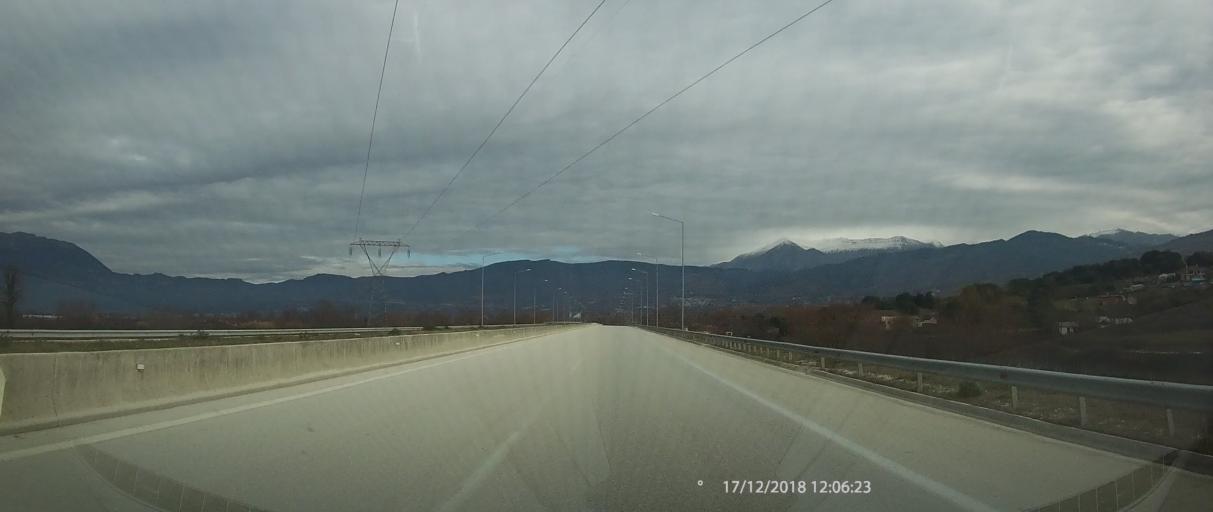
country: GR
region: Epirus
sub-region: Nomos Ioanninon
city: Koutselio
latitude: 39.6061
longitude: 20.9345
